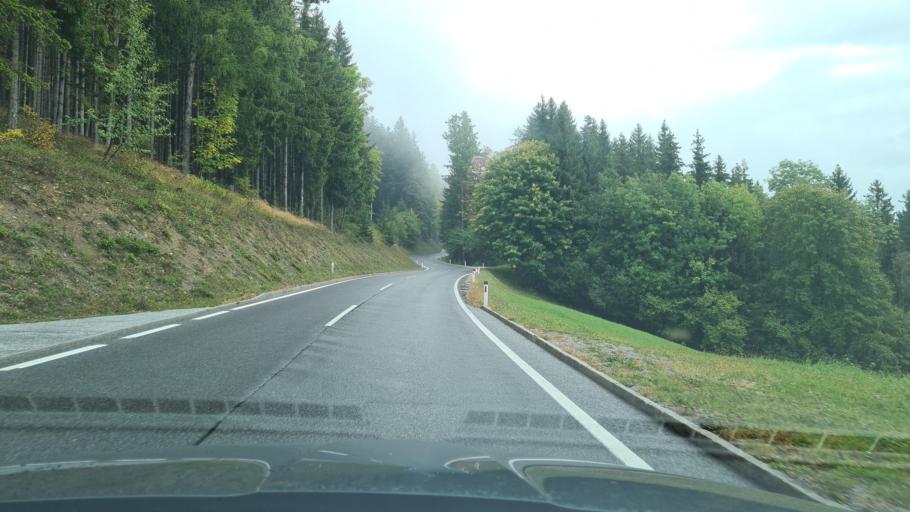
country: AT
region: Styria
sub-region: Politischer Bezirk Weiz
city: Passail
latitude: 47.2962
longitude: 15.4775
